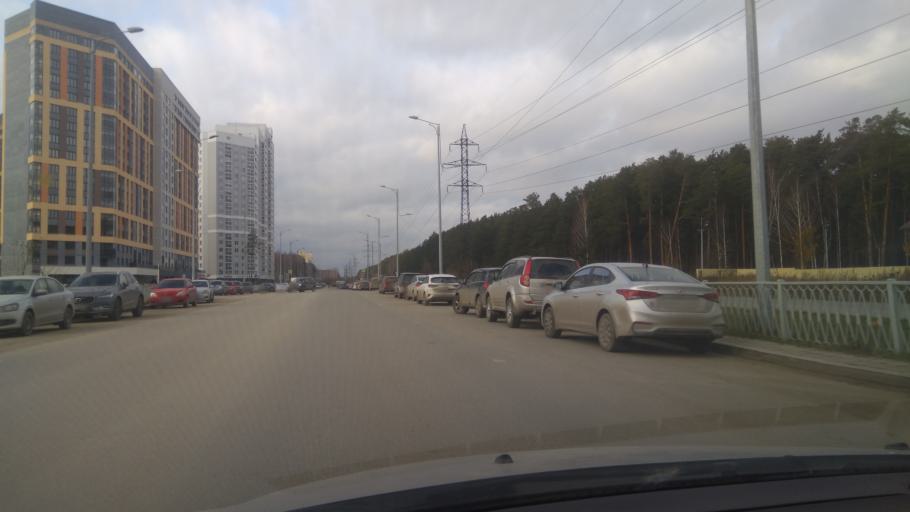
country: RU
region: Sverdlovsk
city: Sovkhoznyy
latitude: 56.7841
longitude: 60.5521
